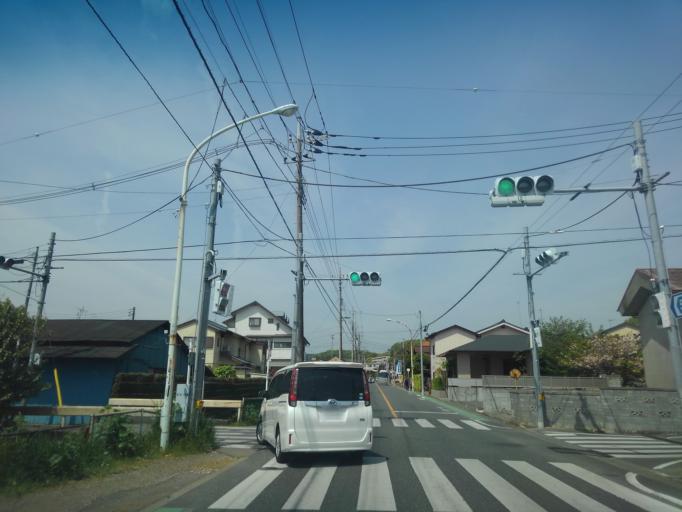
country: JP
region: Tokyo
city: Higashimurayama-shi
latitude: 35.7569
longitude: 139.4088
